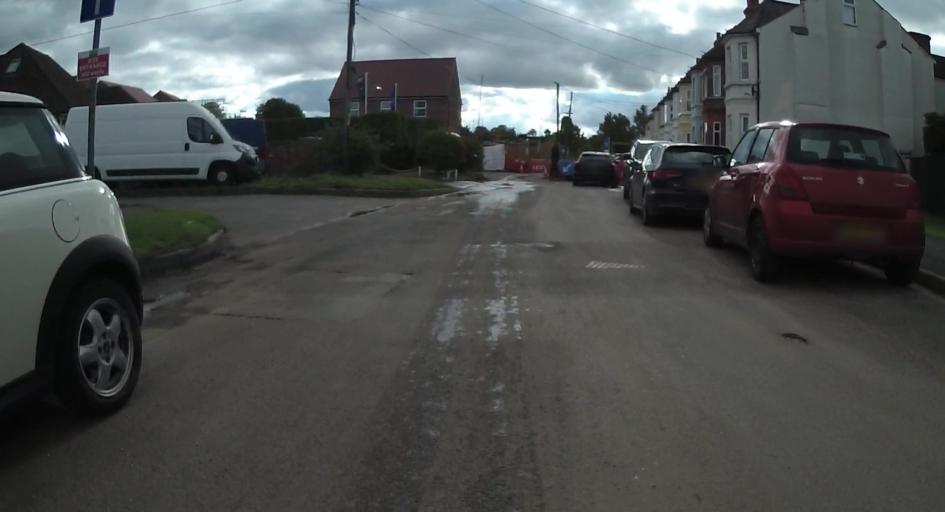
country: GB
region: England
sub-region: Surrey
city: Seale
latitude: 51.2324
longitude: -0.7330
